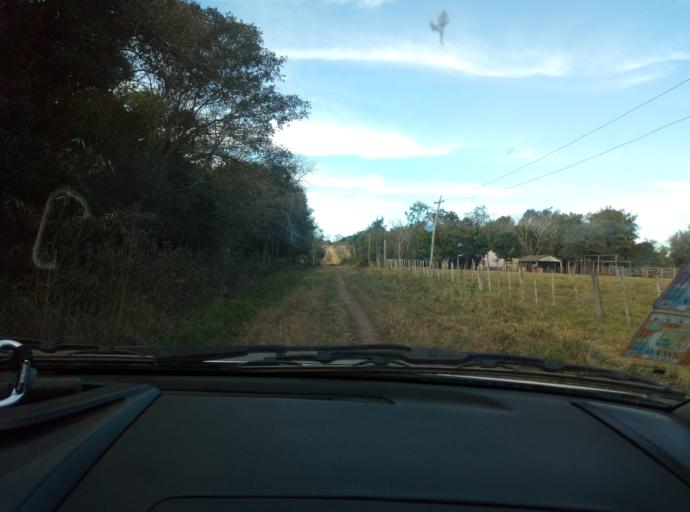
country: PY
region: Caaguazu
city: Carayao
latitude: -25.1715
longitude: -56.2910
